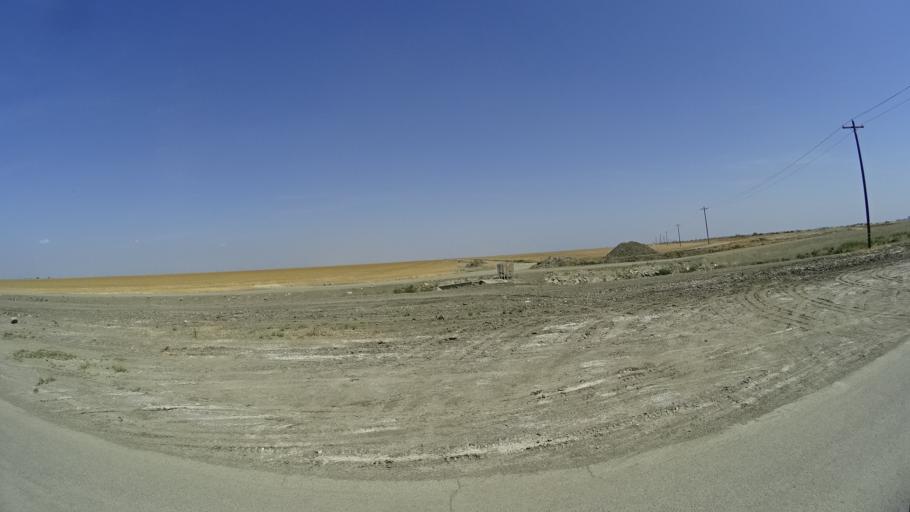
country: US
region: California
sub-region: Kings County
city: Stratford
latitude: 36.1379
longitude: -119.8877
